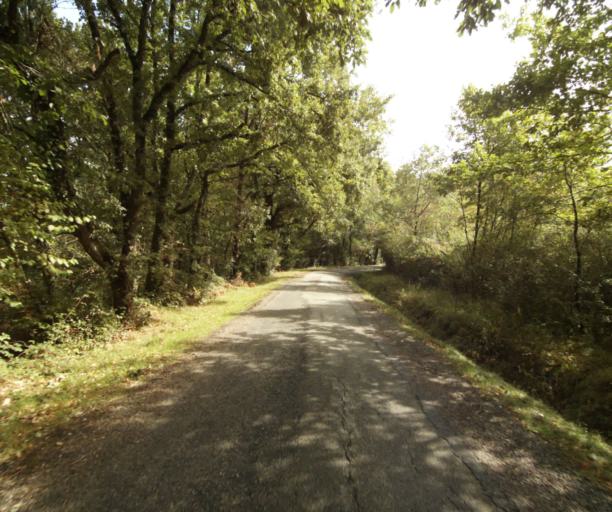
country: FR
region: Midi-Pyrenees
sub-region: Departement du Tarn-et-Garonne
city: Beaumont-de-Lomagne
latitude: 43.8756
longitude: 1.0854
